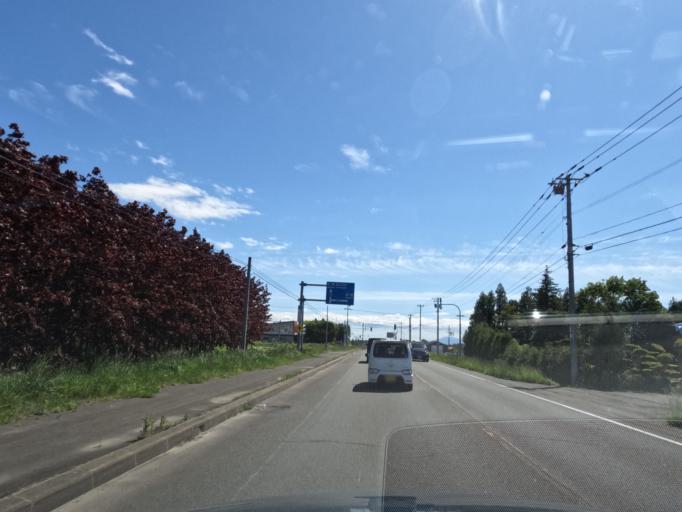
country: JP
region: Hokkaido
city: Kitahiroshima
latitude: 43.0317
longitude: 141.7151
